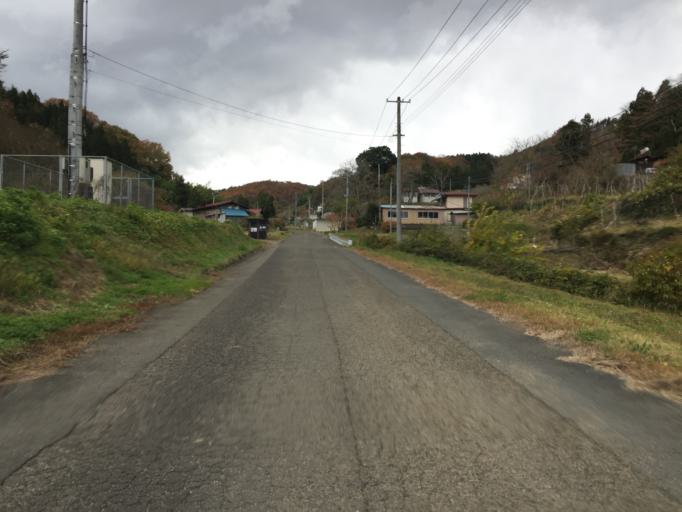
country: JP
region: Fukushima
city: Fukushima-shi
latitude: 37.7334
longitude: 140.5365
